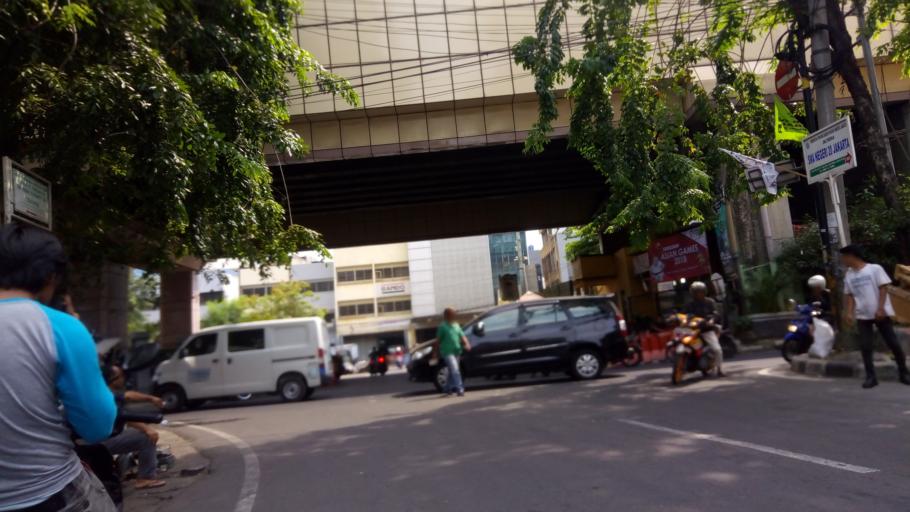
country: ID
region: Jakarta Raya
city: Jakarta
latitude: -6.1596
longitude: 106.8278
